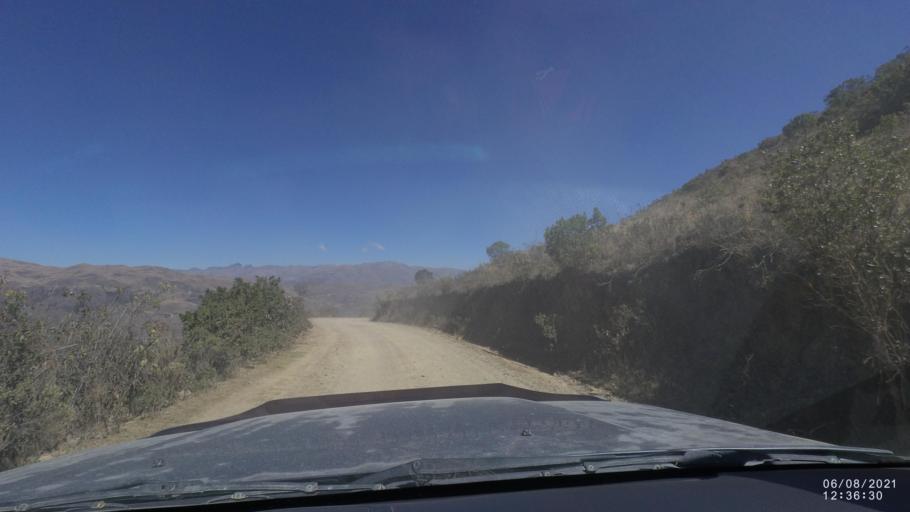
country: BO
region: Cochabamba
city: Colchani
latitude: -16.7785
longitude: -66.6545
